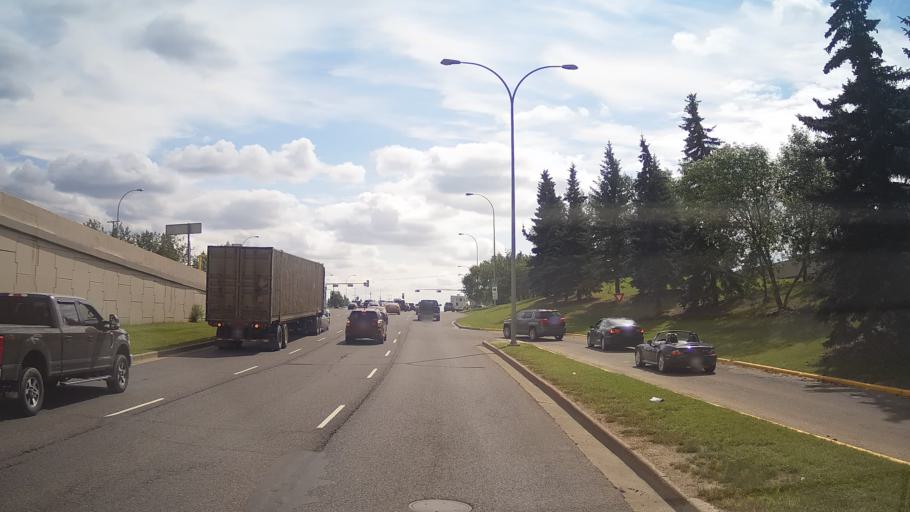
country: CA
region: Alberta
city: St. Albert
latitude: 53.5214
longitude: -113.6157
